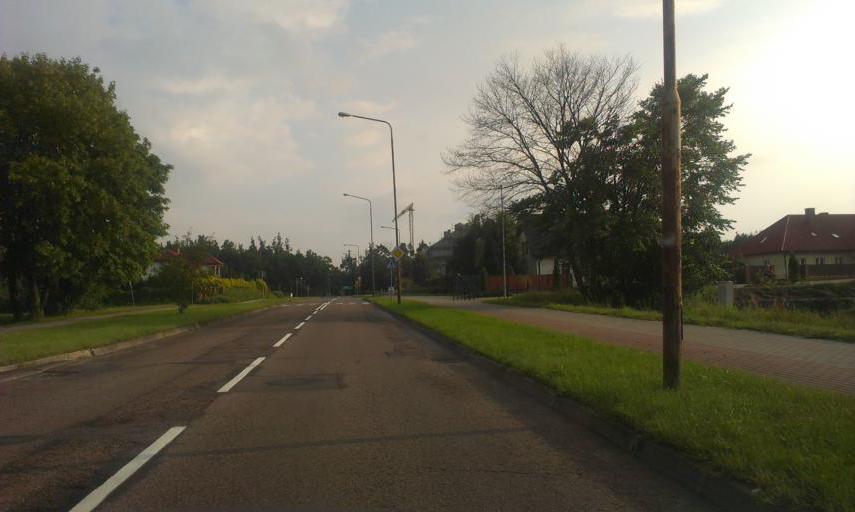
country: PL
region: West Pomeranian Voivodeship
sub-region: Powiat szczecinecki
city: Szczecinek
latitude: 53.7184
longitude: 16.6596
